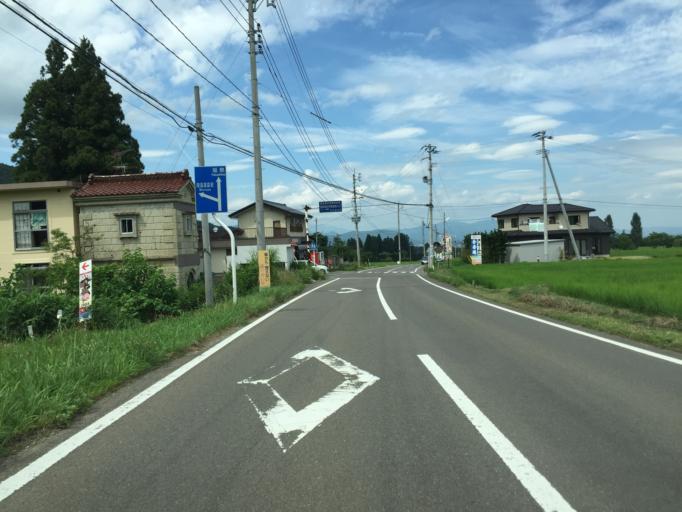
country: JP
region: Fukushima
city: Fukushima-shi
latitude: 37.7148
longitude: 140.3522
